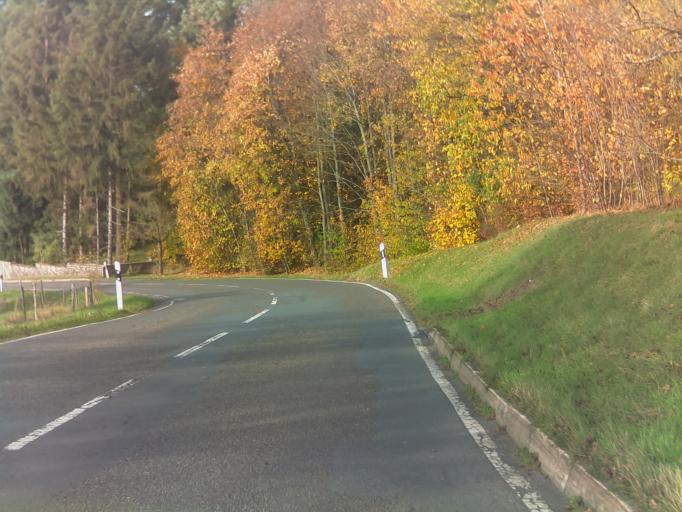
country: DE
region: Baden-Wuerttemberg
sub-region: Karlsruhe Region
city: Rosenberg
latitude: 49.3999
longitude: 9.5155
